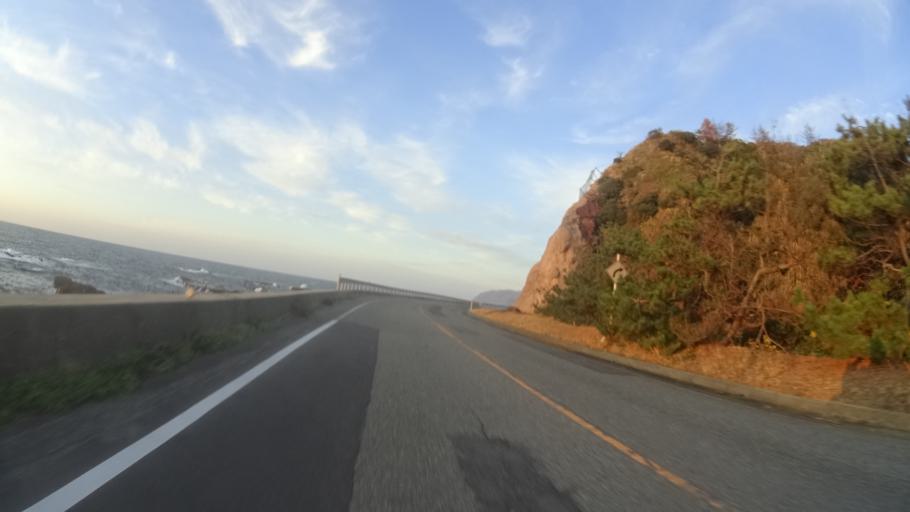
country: JP
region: Ishikawa
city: Nanao
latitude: 37.2442
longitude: 136.7032
